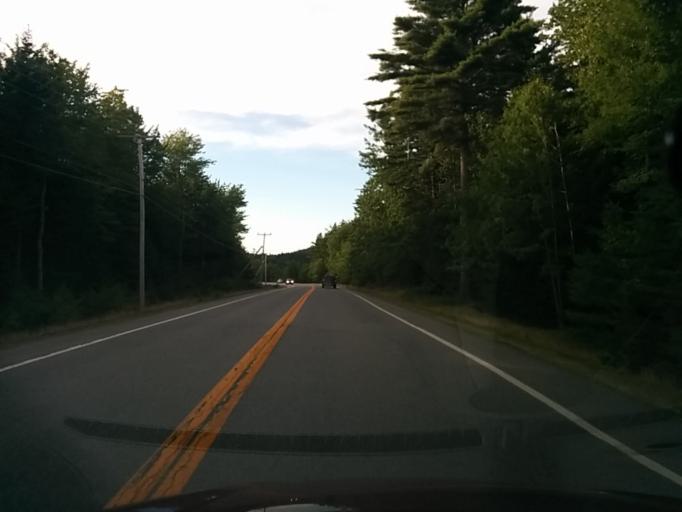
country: US
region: Maine
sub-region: Hancock County
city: Tremont
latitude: 44.3157
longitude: -68.2868
